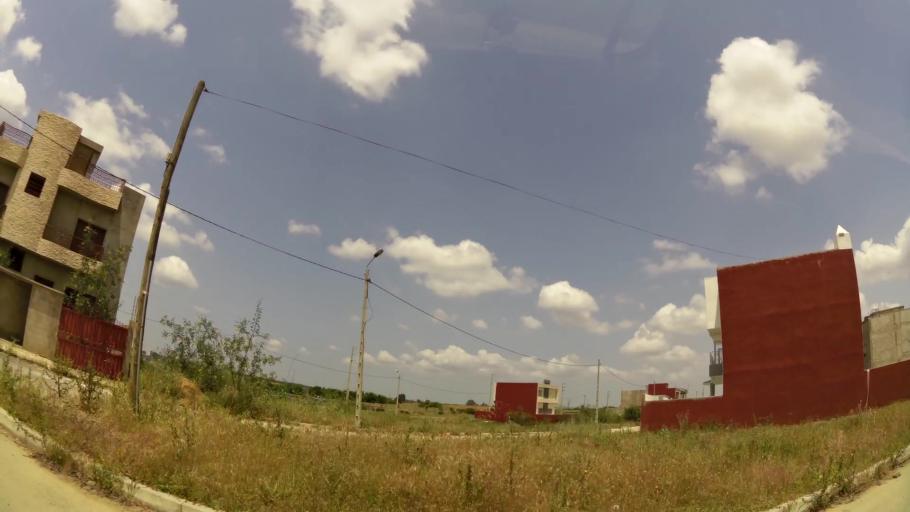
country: MA
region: Rabat-Sale-Zemmour-Zaer
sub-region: Khemisset
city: Tiflet
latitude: 34.0035
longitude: -6.5416
